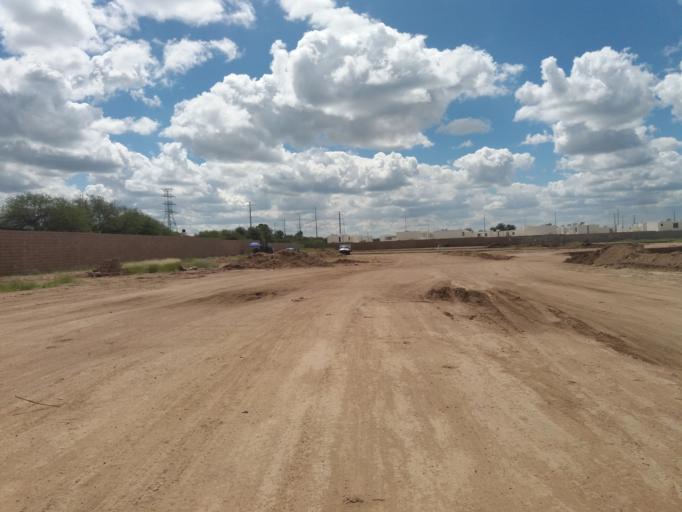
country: MX
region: Aguascalientes
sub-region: Aguascalientes
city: San Sebastian [Fraccionamiento]
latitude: 21.8212
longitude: -102.2721
